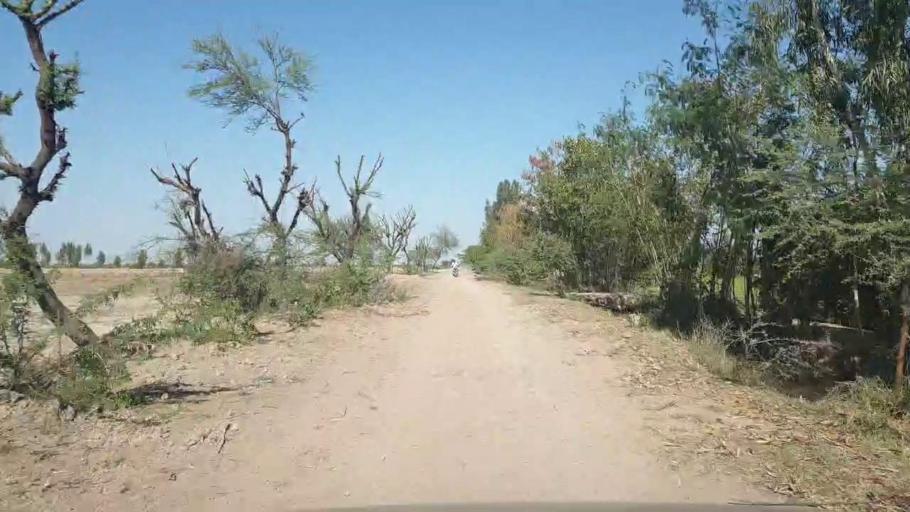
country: PK
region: Sindh
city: Dhoro Naro
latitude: 25.3982
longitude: 69.5933
